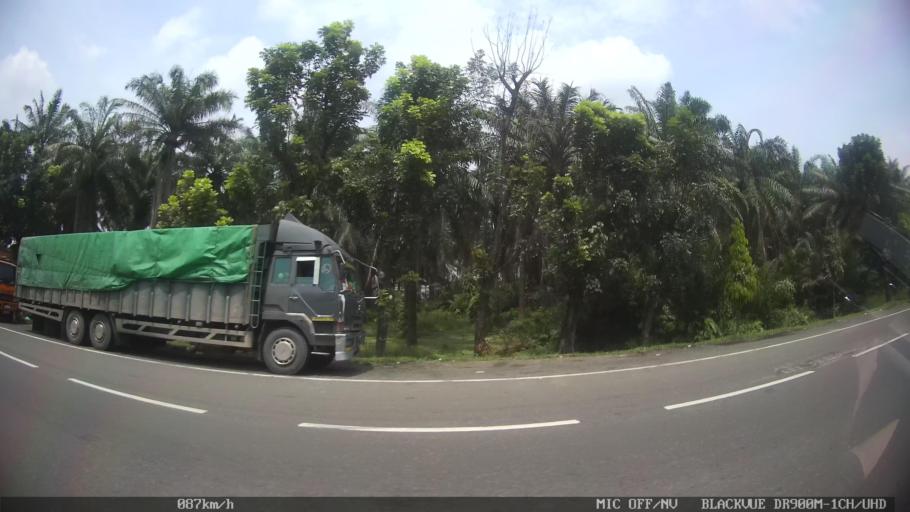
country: ID
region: North Sumatra
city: Labuhan Deli
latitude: 3.6726
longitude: 98.6804
